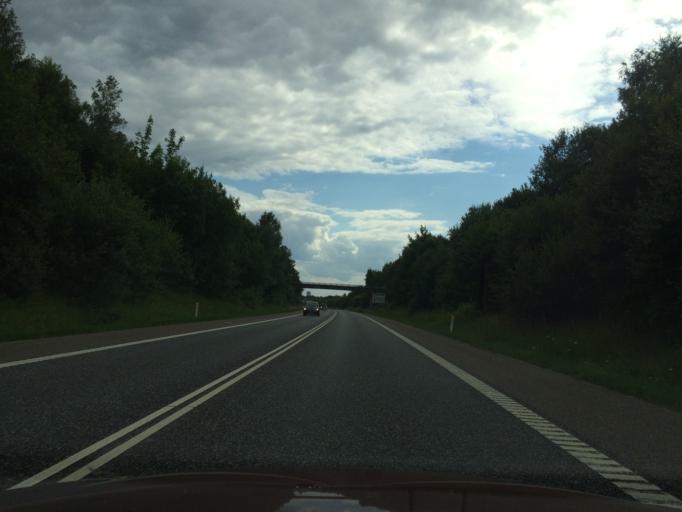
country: DK
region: Central Jutland
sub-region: Syddjurs Kommune
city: Hornslet
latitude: 56.2973
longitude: 10.3387
